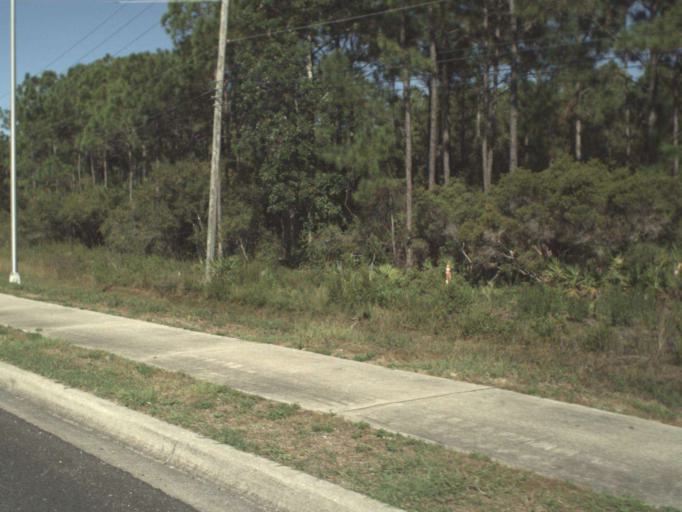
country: US
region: Florida
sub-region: Walton County
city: Miramar Beach
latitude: 30.3761
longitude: -86.3025
